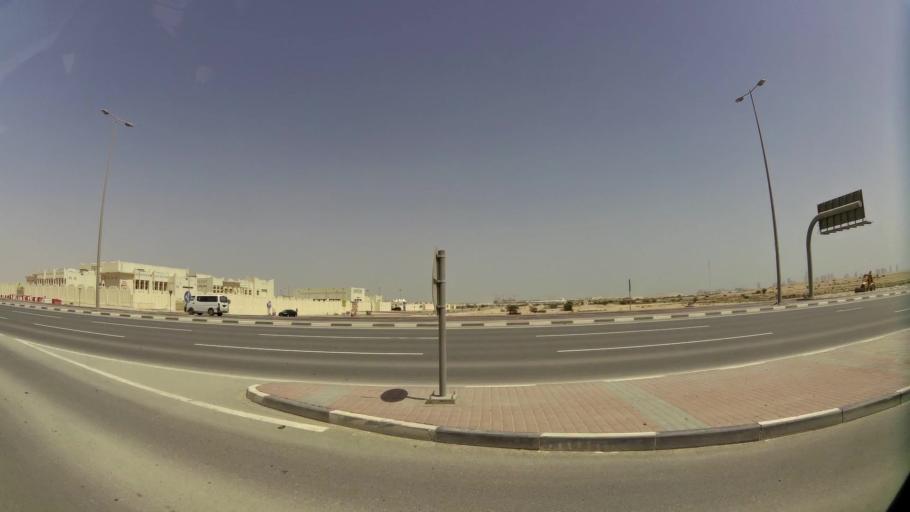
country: QA
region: Baladiyat Umm Salal
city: Umm Salal Muhammad
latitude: 25.4027
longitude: 51.4564
